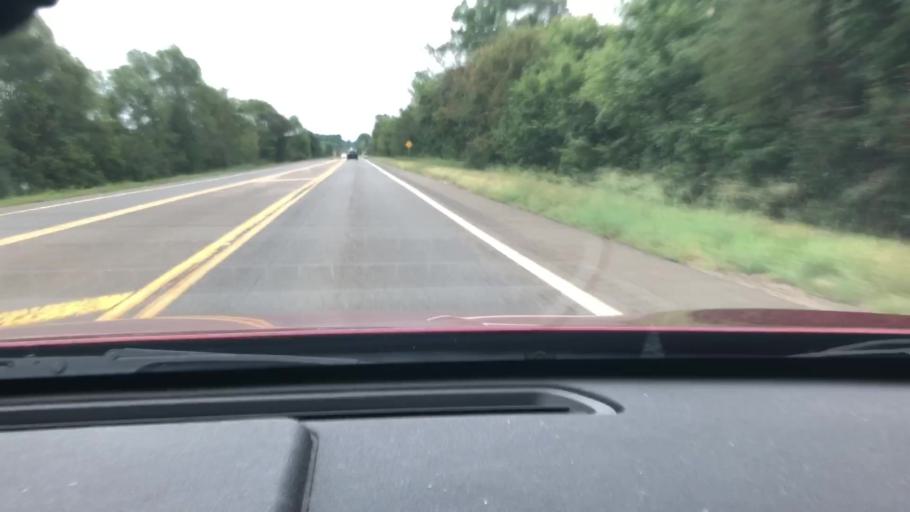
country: US
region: Arkansas
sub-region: Lafayette County
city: Lewisville
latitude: 33.3575
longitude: -93.6403
